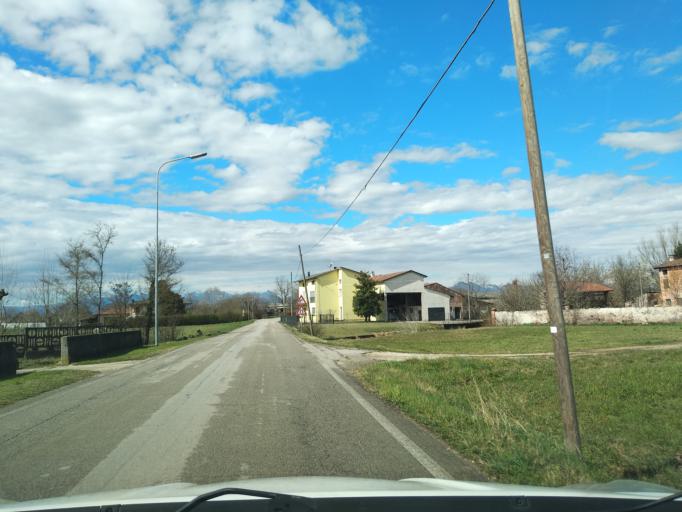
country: IT
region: Veneto
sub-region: Provincia di Vicenza
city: Vigardolo
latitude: 45.6097
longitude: 11.6043
